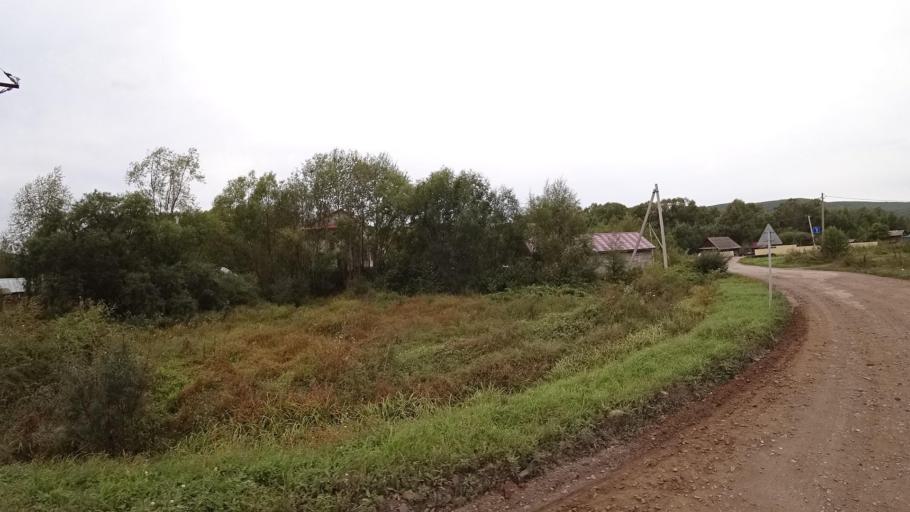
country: RU
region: Jewish Autonomous Oblast
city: Khingansk
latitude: 49.0248
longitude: 131.0540
